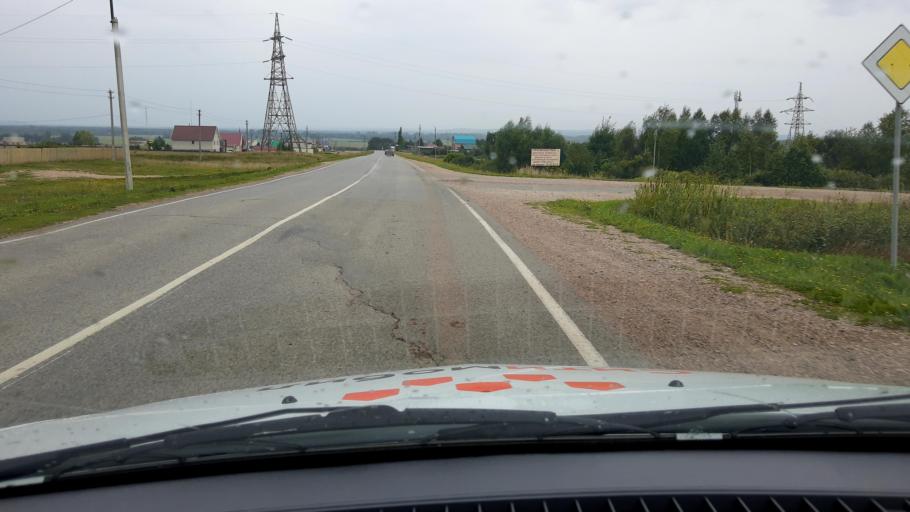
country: RU
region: Bashkortostan
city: Krasnaya Gorka
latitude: 55.1844
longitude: 56.6811
